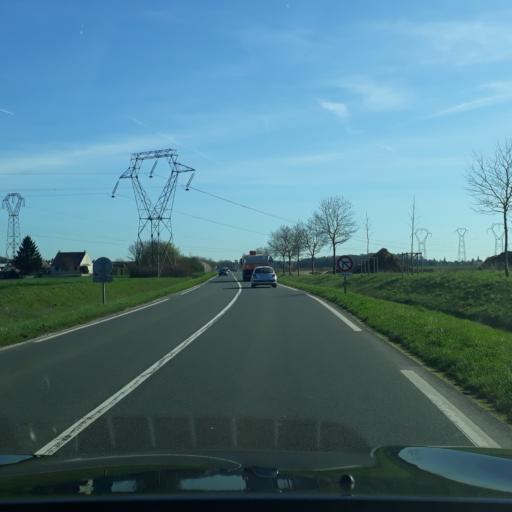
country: FR
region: Ile-de-France
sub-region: Departement de l'Essonne
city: Ballancourt-sur-Essonne
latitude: 48.5435
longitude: 2.4001
